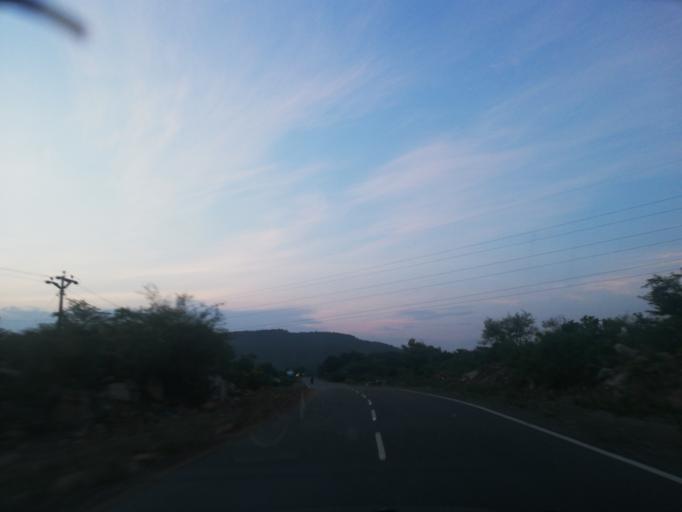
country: IN
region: Andhra Pradesh
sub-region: Guntur
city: Macherla
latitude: 16.6673
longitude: 79.2823
